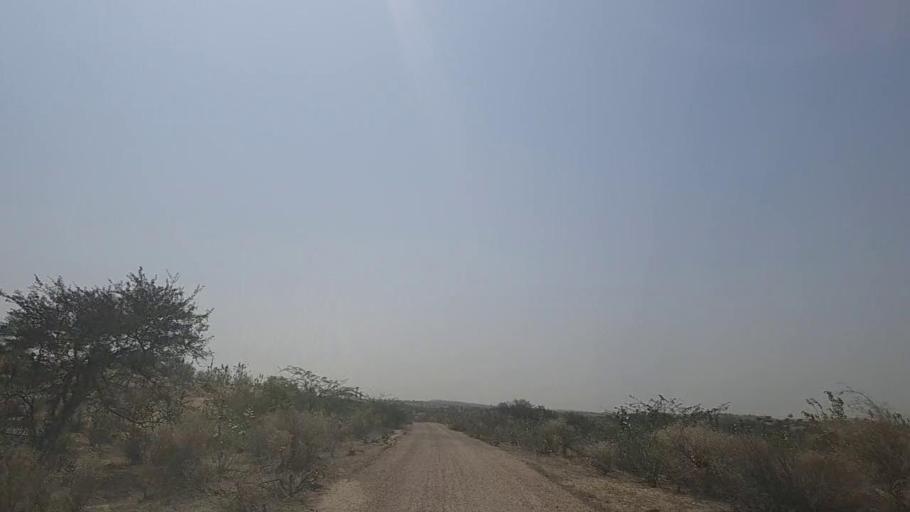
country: PK
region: Sindh
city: Naukot
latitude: 24.8136
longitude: 69.4752
